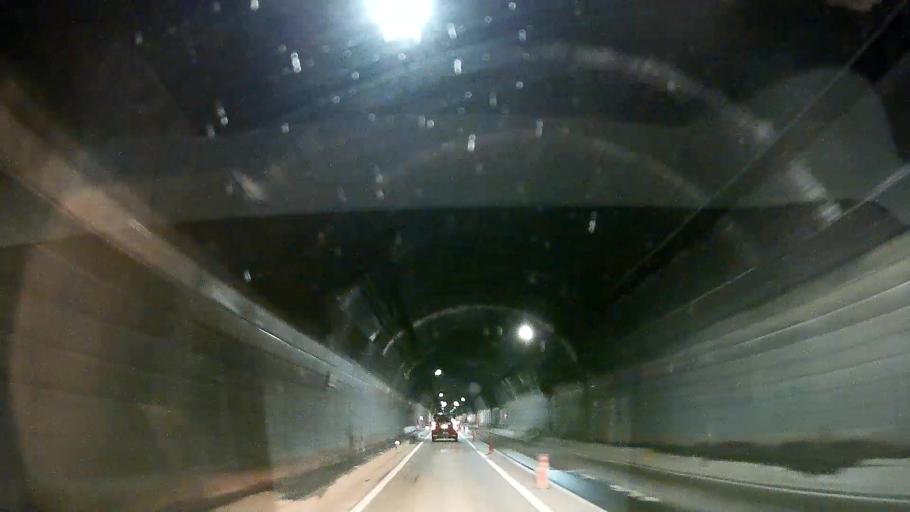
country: JP
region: Saitama
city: Chichibu
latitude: 35.9520
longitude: 139.1747
